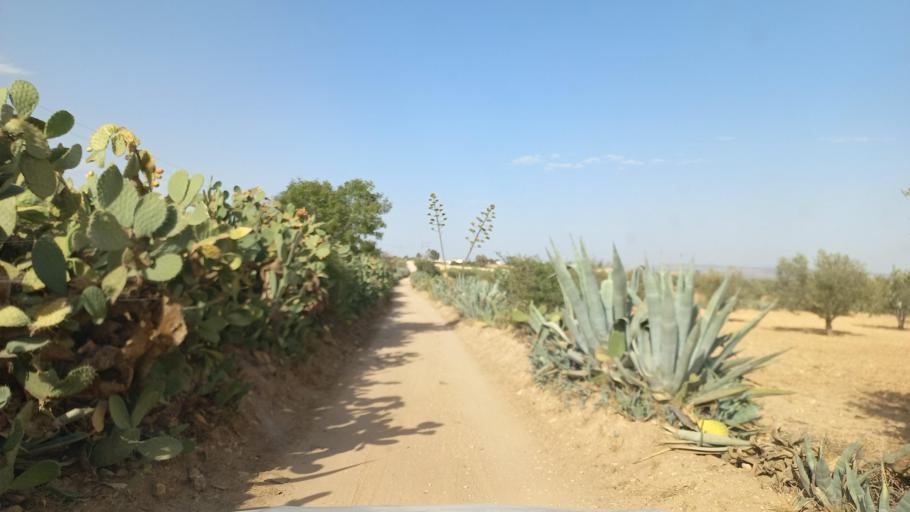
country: TN
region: Al Qasrayn
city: Kasserine
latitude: 35.2524
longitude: 8.9304
